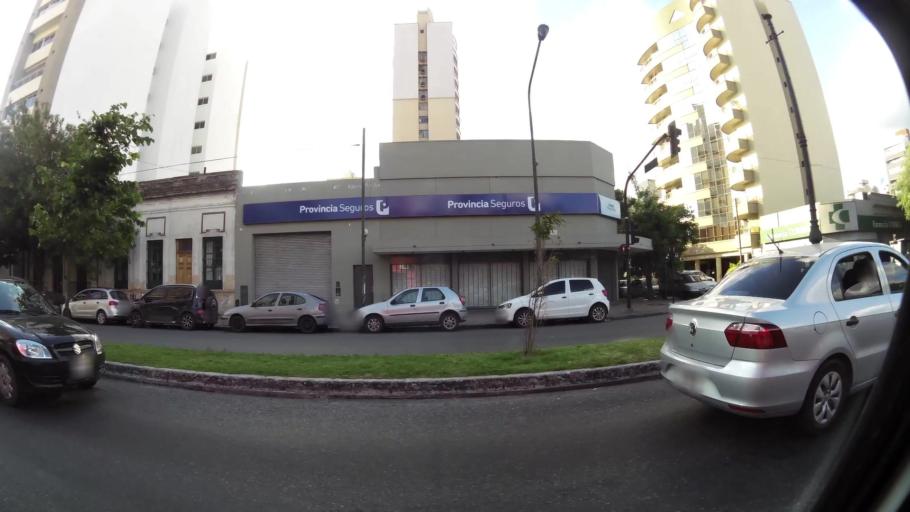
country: AR
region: Buenos Aires
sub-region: Partido de La Plata
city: La Plata
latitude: -34.9136
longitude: -57.9584
